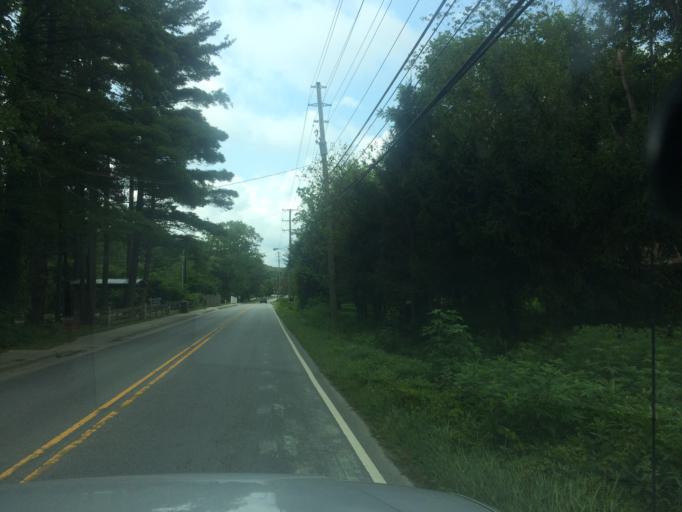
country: US
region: North Carolina
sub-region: Henderson County
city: Balfour
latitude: 35.3295
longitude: -82.4745
